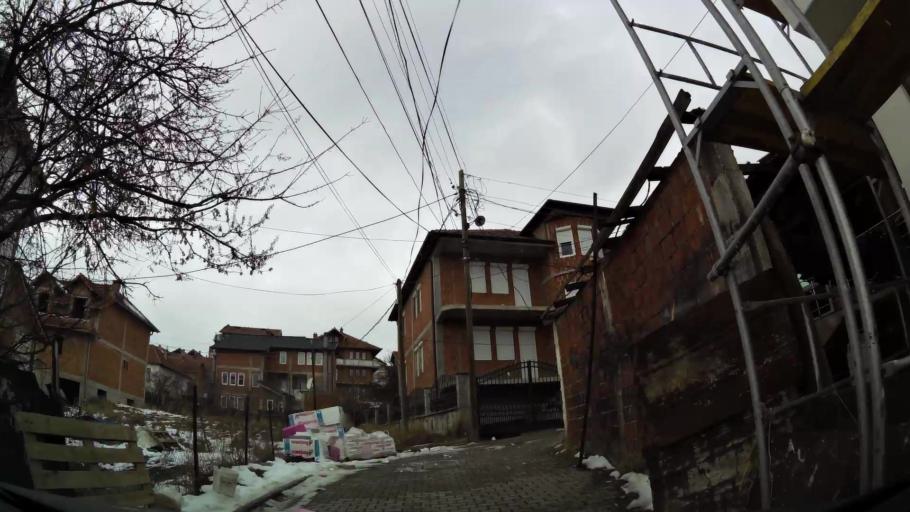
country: XK
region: Pristina
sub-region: Komuna e Prishtines
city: Pristina
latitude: 42.6739
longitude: 21.1563
